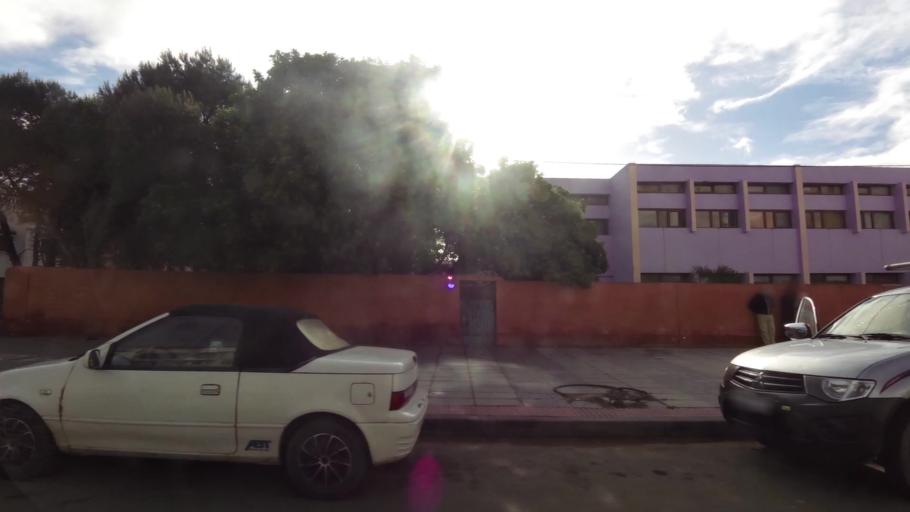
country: MA
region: Doukkala-Abda
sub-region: El-Jadida
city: El Jadida
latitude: 33.2502
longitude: -8.5180
